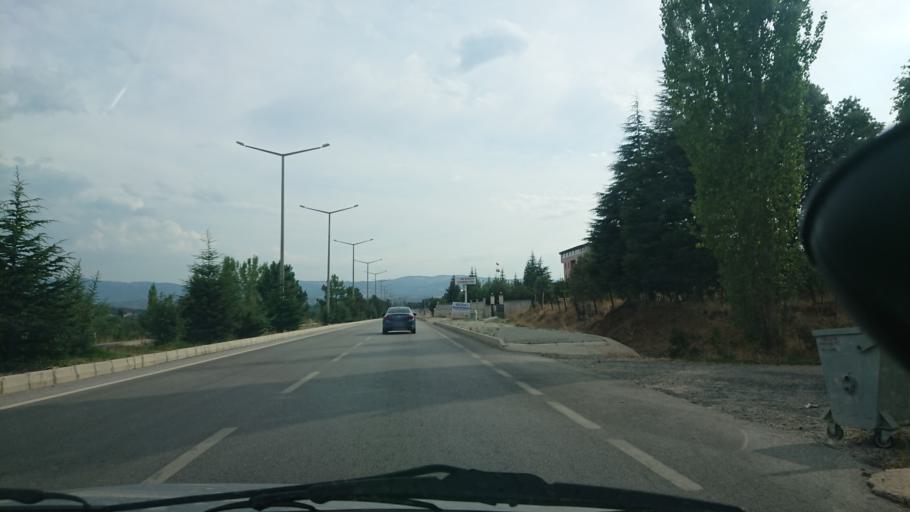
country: TR
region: Kuetahya
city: Gediz
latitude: 39.0039
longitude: 29.4048
